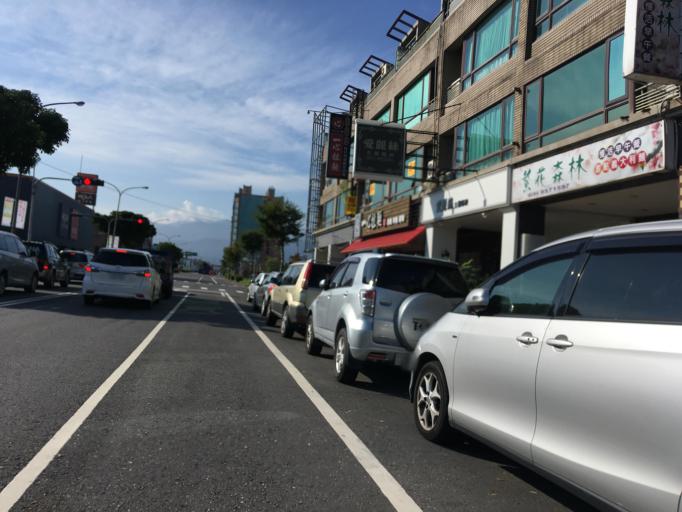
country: TW
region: Taiwan
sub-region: Yilan
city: Yilan
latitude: 24.6807
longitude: 121.7777
